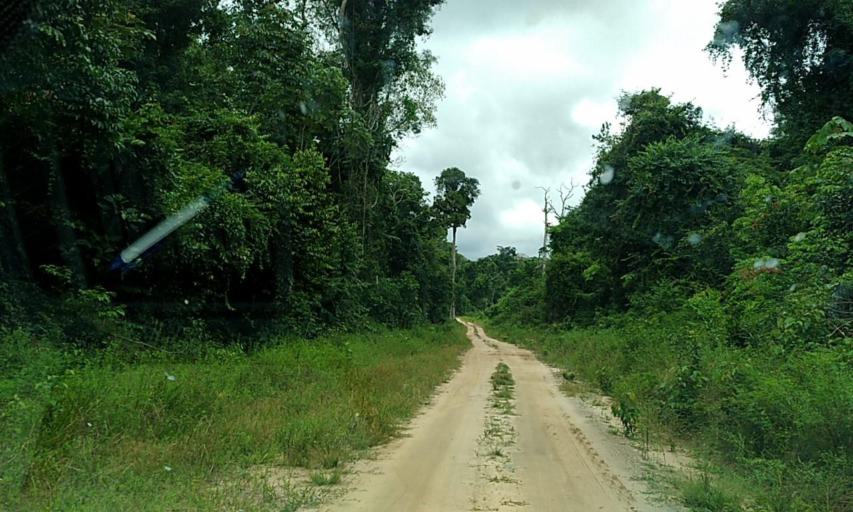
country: BR
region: Para
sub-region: Altamira
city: Altamira
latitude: -3.0490
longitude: -52.9078
